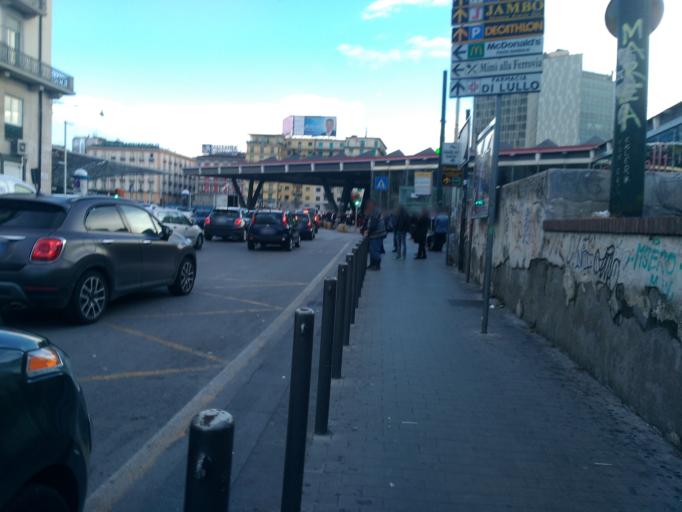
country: IT
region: Campania
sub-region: Provincia di Napoli
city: Napoli
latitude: 40.8515
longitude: 14.2720
